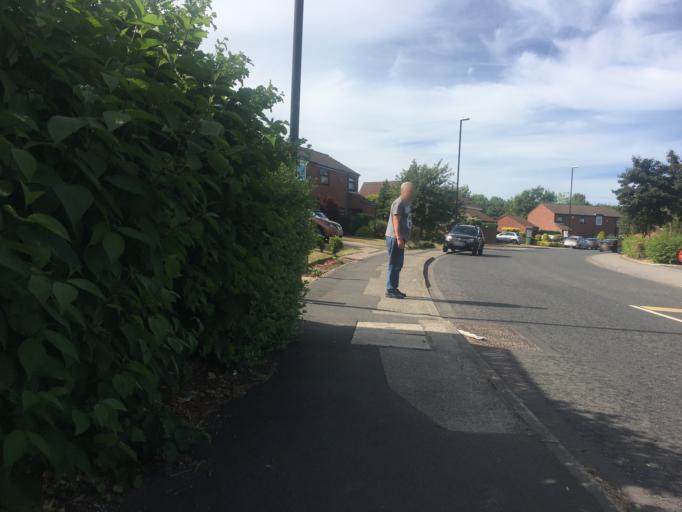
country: GB
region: England
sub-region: Sunderland
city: Washington
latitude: 54.8894
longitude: -1.5407
